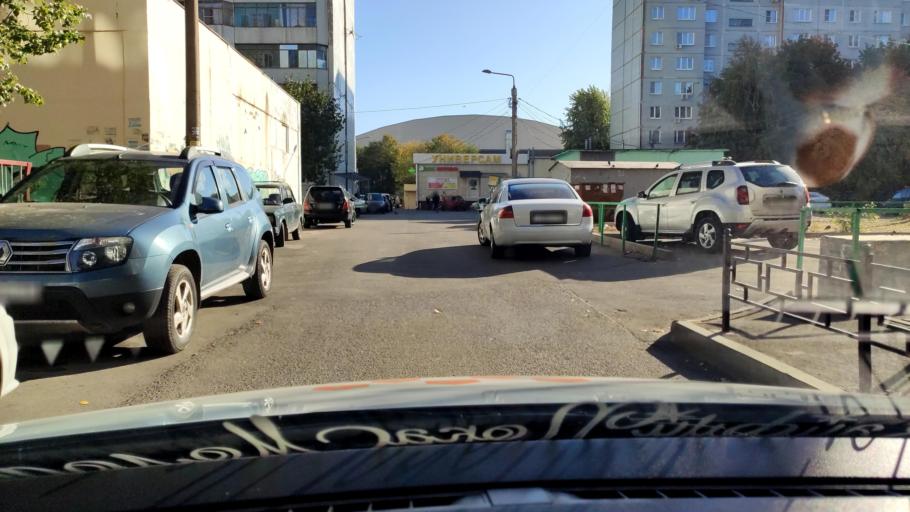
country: RU
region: Voronezj
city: Podgornoye
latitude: 51.7086
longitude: 39.1563
